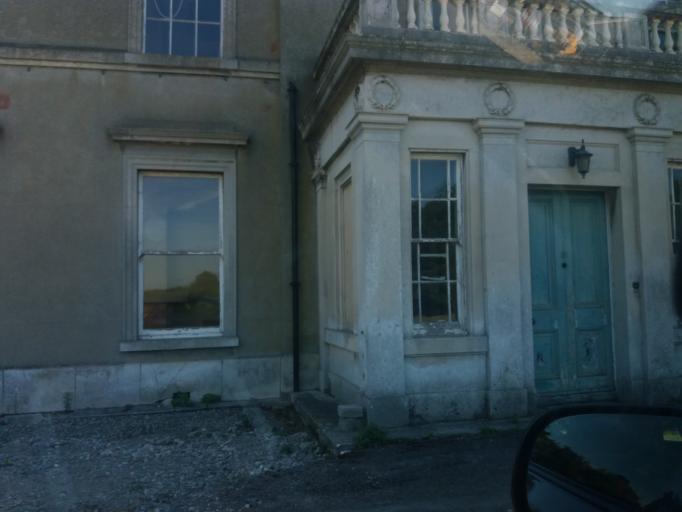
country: IE
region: Leinster
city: Castleknock
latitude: 53.3923
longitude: -6.3576
